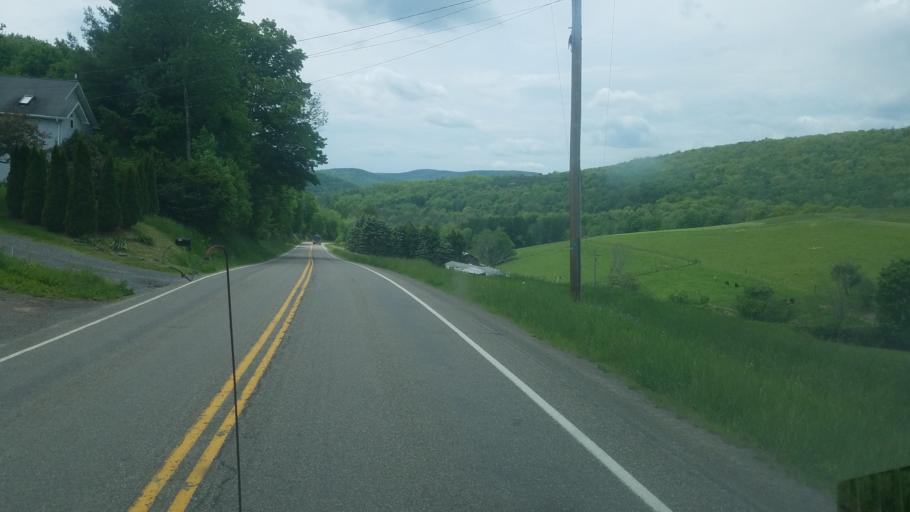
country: US
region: Pennsylvania
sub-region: Tioga County
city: Wellsboro
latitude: 41.7321
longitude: -77.4017
